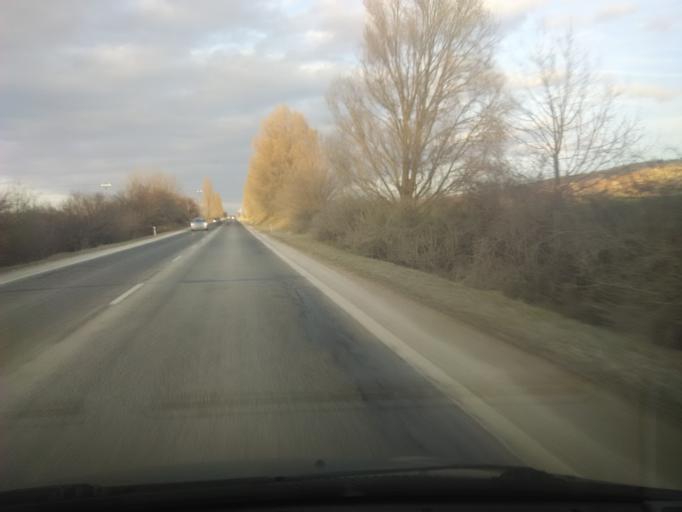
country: SK
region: Nitriansky
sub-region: Okres Nitra
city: Nitra
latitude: 48.3458
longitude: 18.1732
